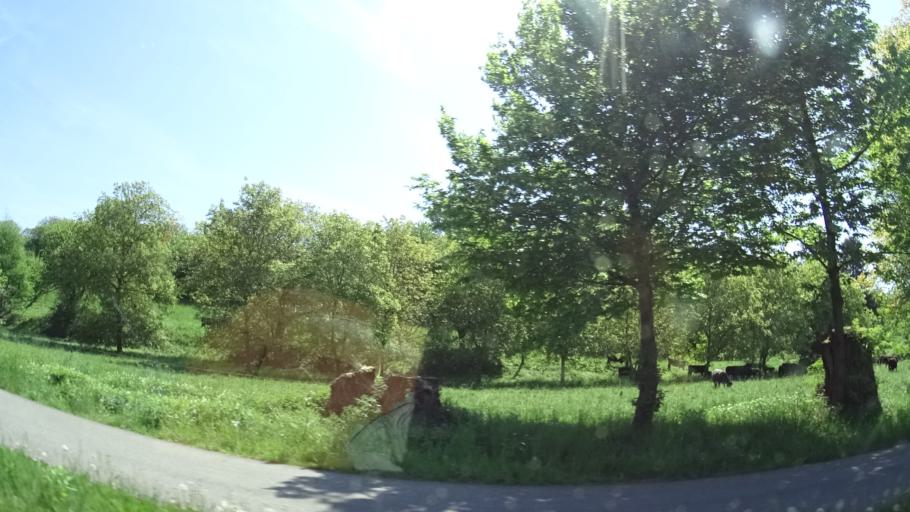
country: DE
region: Baden-Wuerttemberg
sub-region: Karlsruhe Region
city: Malsch
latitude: 48.8873
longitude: 8.3432
